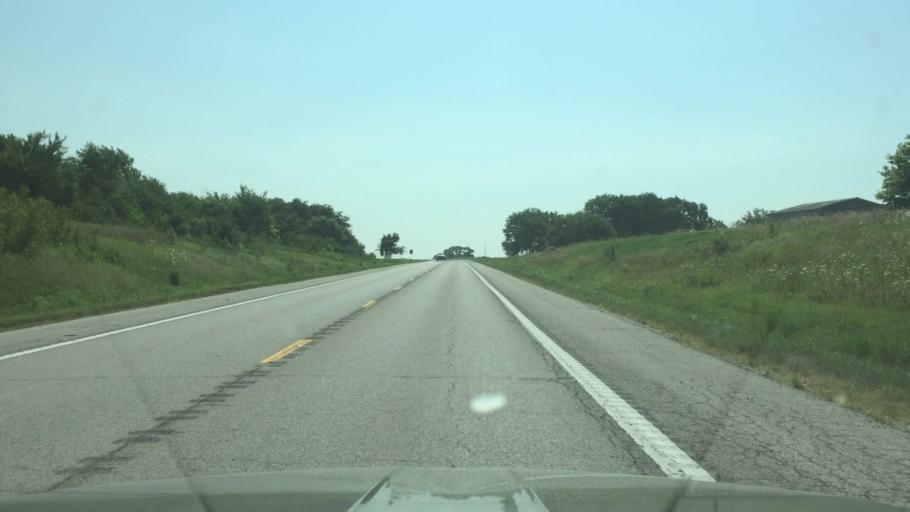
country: US
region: Missouri
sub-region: Pettis County
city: Sedalia
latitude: 38.6921
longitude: -93.0677
